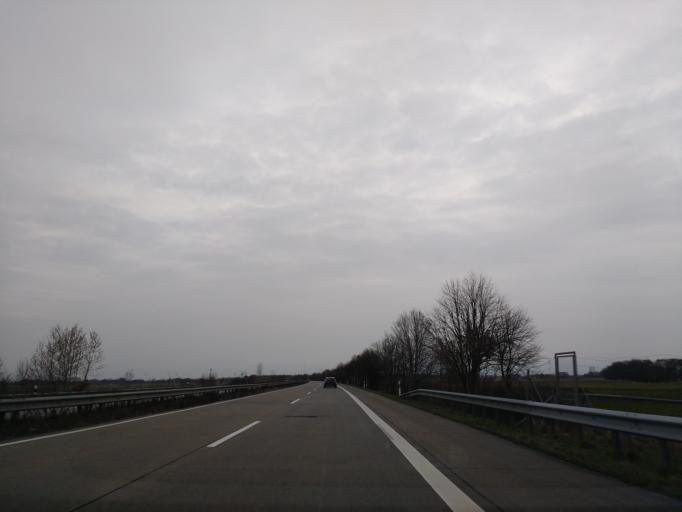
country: DE
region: Lower Saxony
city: Midlum
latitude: 53.7666
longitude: 8.6970
